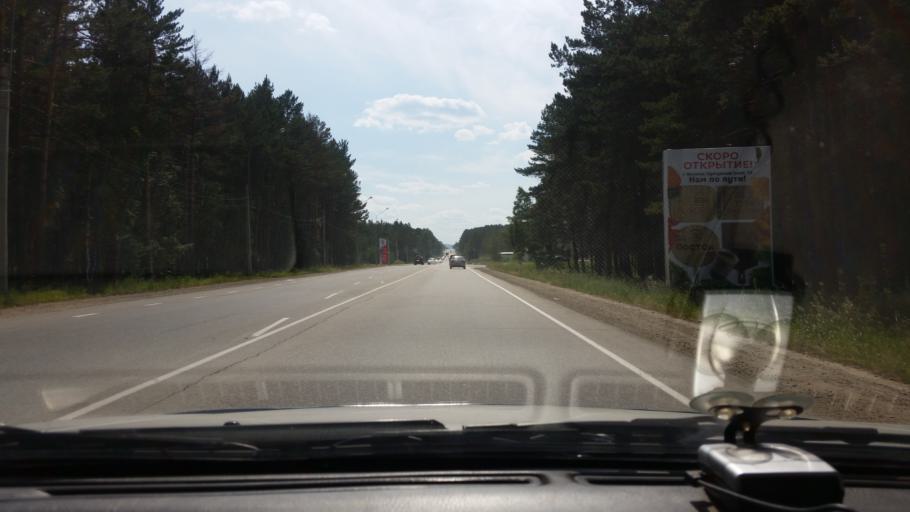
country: RU
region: Irkutsk
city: Shelekhov
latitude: 52.2169
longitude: 104.1270
